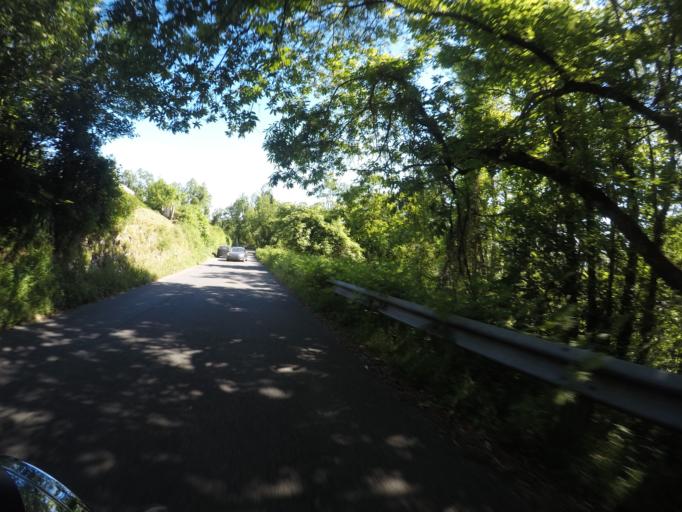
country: IT
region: Liguria
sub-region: Provincia di La Spezia
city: Casano-Dogana-Isola
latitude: 44.1155
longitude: 10.0675
